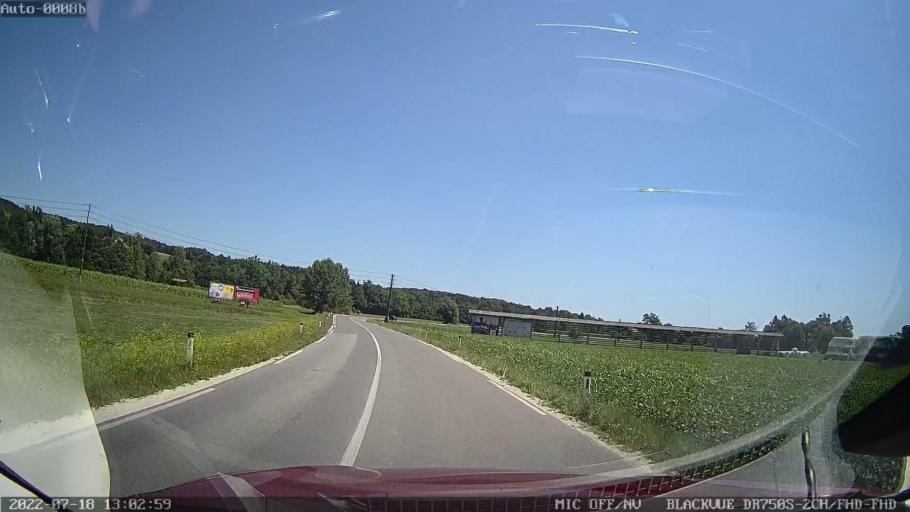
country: SI
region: Brezovica
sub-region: Opstina Ljubljana-Vic-Rudnik
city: Brezovica pri Ljubljani
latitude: 46.0509
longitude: 14.4258
